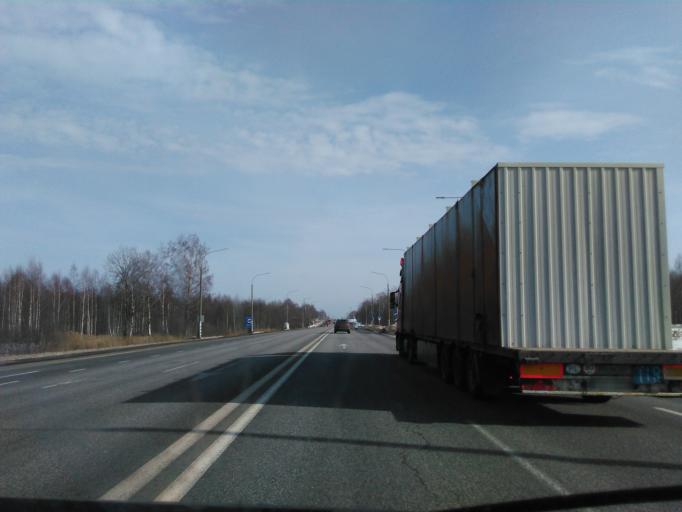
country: BY
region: Vitebsk
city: Dubrowna
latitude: 54.6902
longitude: 30.9538
